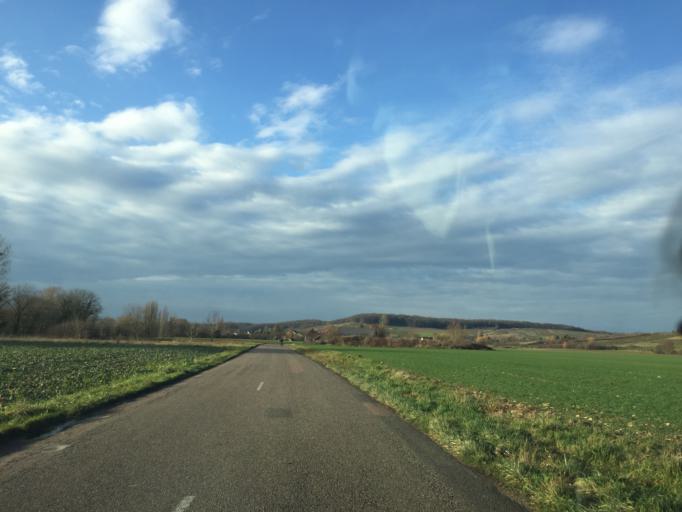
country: FR
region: Franche-Comte
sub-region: Departement du Jura
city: Arbois
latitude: 46.9167
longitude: 5.7617
